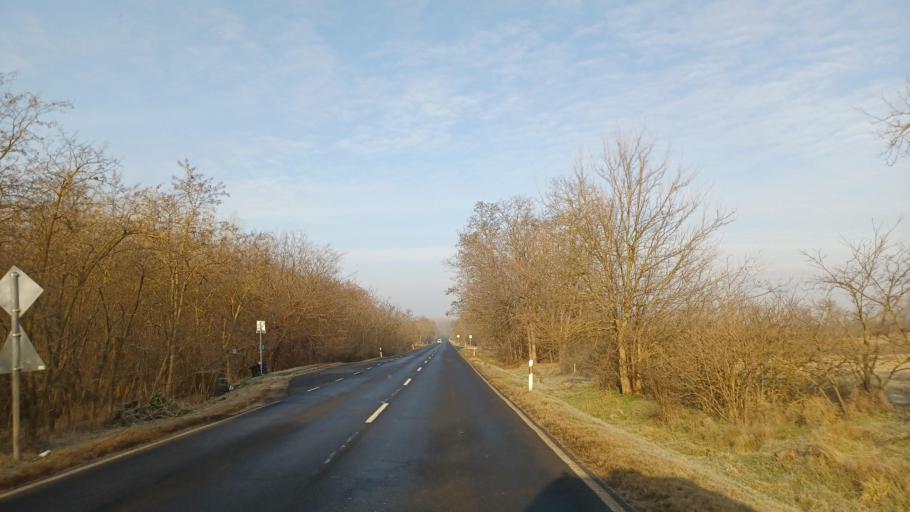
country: HU
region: Fejer
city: Cece
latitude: 46.7397
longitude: 18.6543
